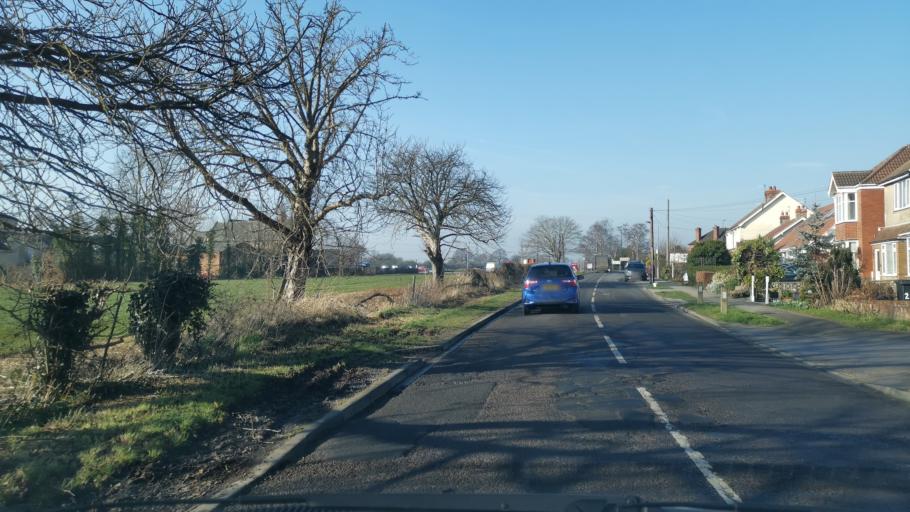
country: GB
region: England
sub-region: City of York
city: Huntington
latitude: 53.9877
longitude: -1.0275
